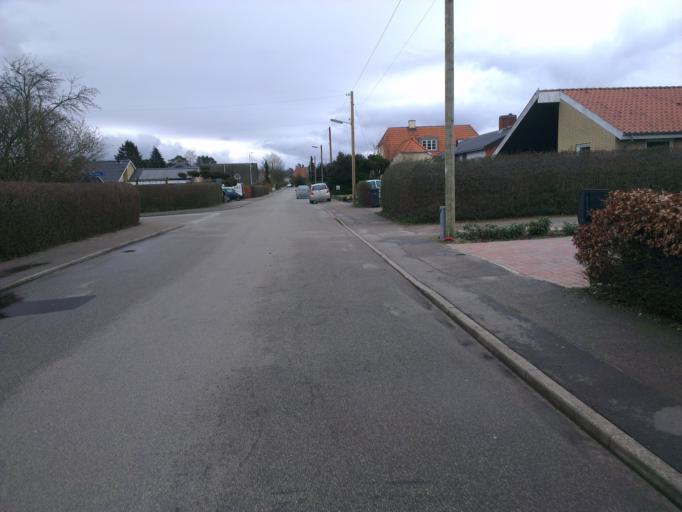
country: DK
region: Capital Region
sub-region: Frederikssund Kommune
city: Frederikssund
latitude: 55.8259
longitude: 12.0690
